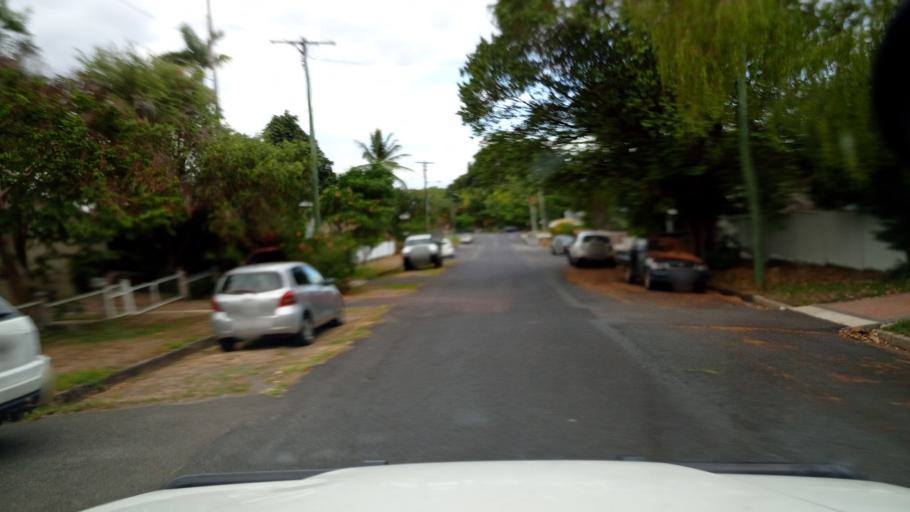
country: AU
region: Queensland
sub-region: Cairns
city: Redlynch
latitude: -16.8768
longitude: 145.7329
